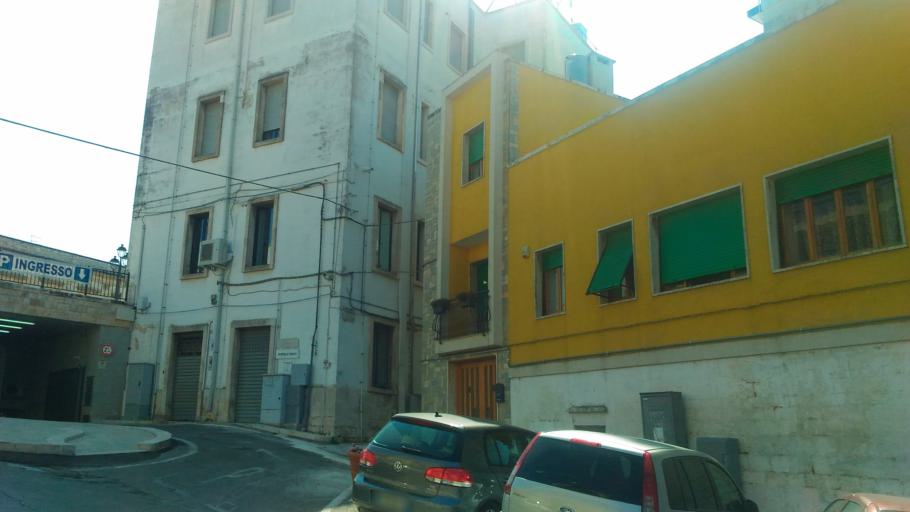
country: IT
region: Apulia
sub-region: Provincia di Bari
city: Locorotondo
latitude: 40.7547
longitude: 17.3261
